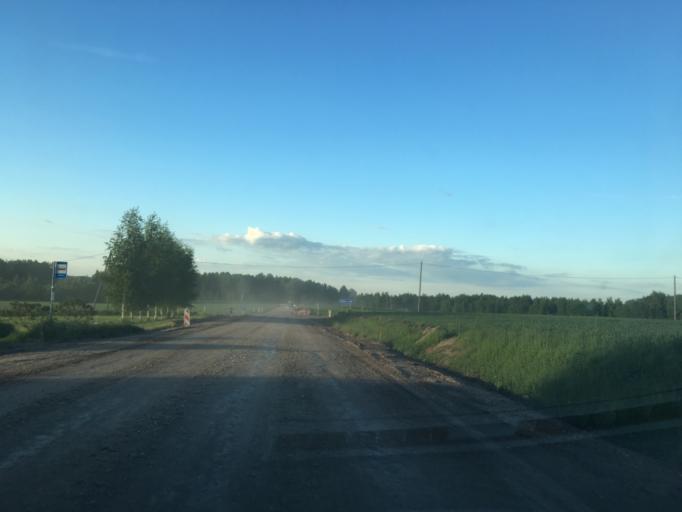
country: EE
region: Tartu
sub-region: UElenurme vald
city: Ulenurme
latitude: 58.2385
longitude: 26.6576
